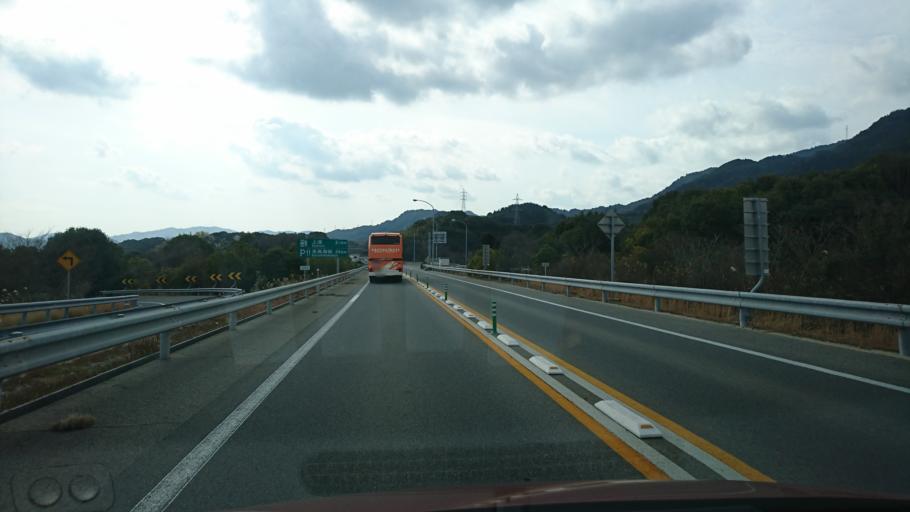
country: JP
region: Hiroshima
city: Innoshima
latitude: 34.2506
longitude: 133.0491
